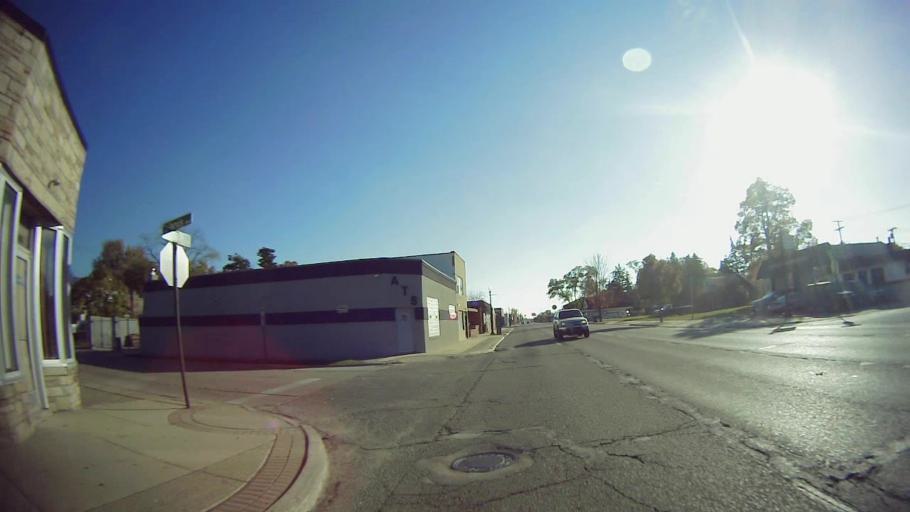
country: US
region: Michigan
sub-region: Oakland County
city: Hazel Park
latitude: 42.4565
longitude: -83.1035
